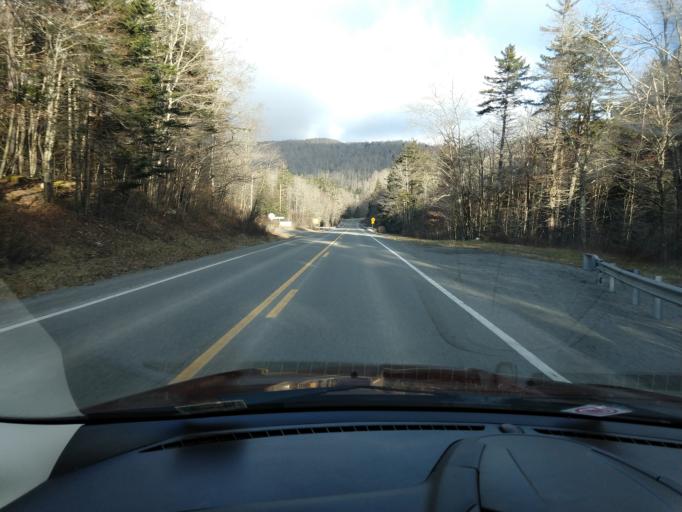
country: US
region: West Virginia
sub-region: Randolph County
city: Elkins
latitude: 38.6162
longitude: -79.8695
